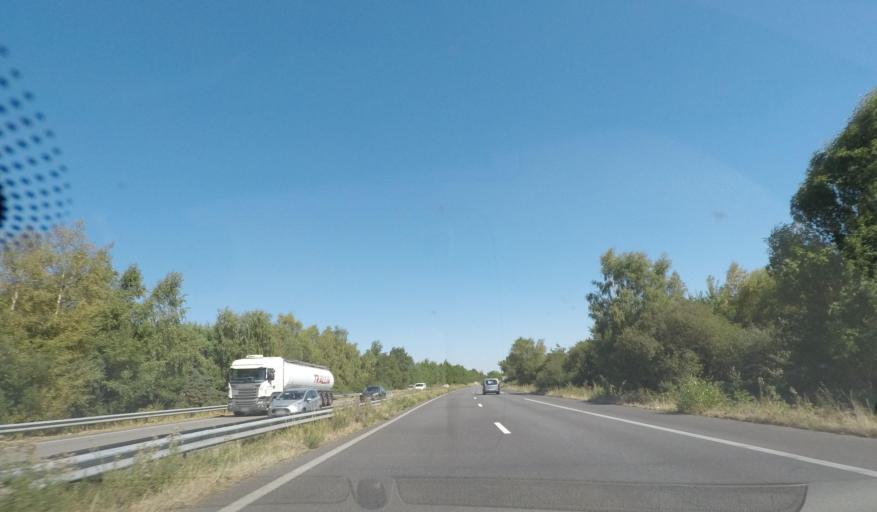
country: FR
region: Pays de la Loire
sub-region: Departement de la Loire-Atlantique
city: Missillac
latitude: 47.4702
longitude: -2.1644
